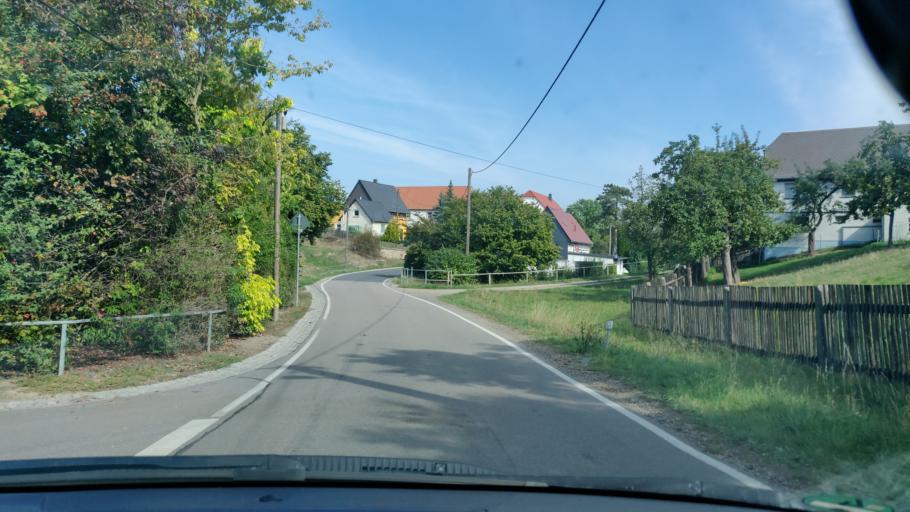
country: DE
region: Saxony
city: Konigsfeld
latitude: 51.0749
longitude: 12.7433
